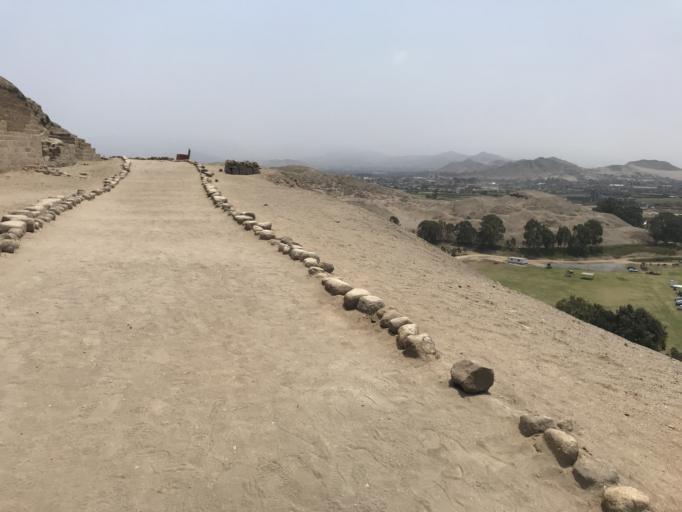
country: PE
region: Lima
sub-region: Lima
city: Punta Hermosa
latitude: -12.2635
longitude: -76.9009
